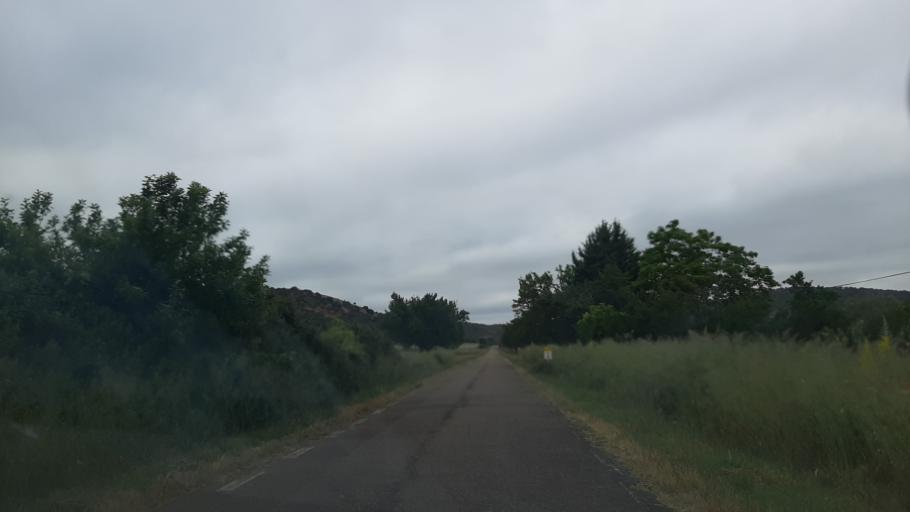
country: ES
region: Castille and Leon
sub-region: Provincia de Salamanca
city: Pastores
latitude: 40.5553
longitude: -6.4873
